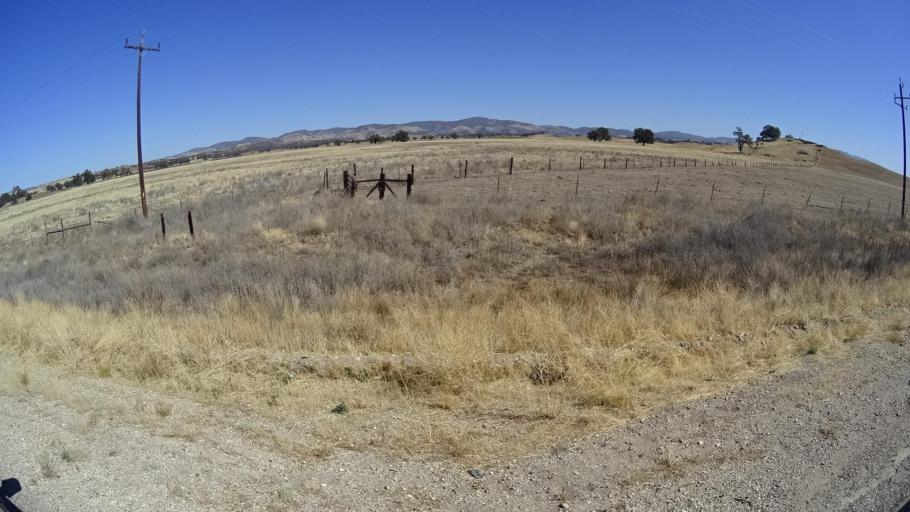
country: US
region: California
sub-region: Monterey County
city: King City
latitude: 35.9513
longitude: -121.1473
